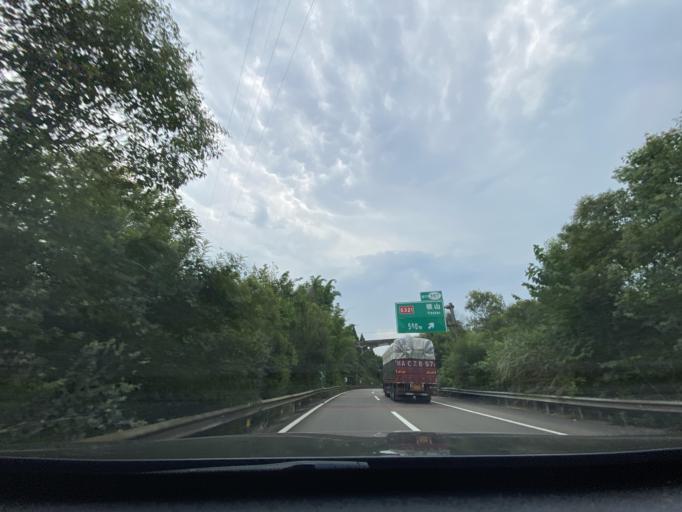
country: CN
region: Sichuan
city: Chonglong
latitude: 29.6809
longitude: 104.9551
